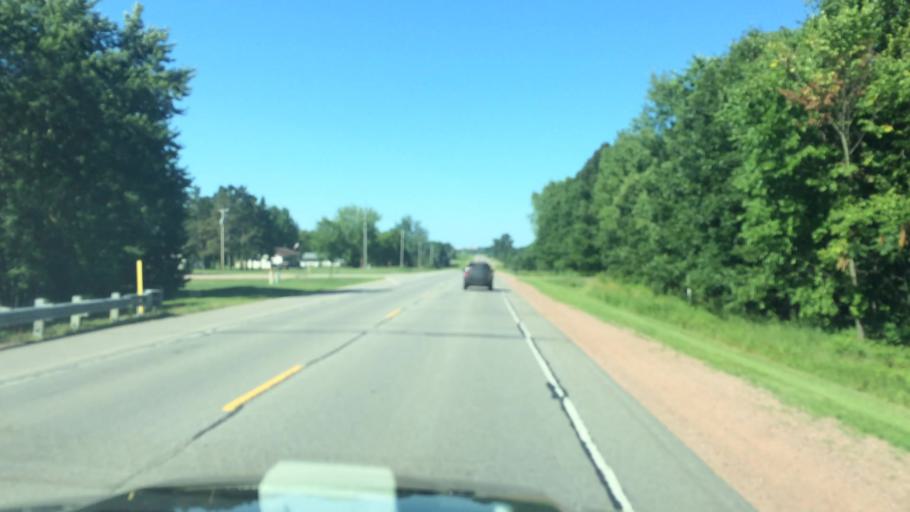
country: US
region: Wisconsin
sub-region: Wood County
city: Marshfield
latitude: 44.7149
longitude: -90.1124
